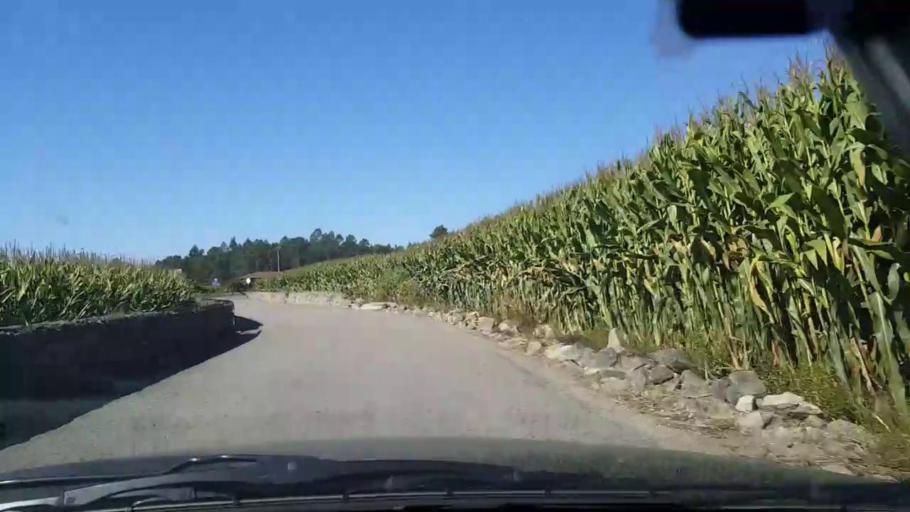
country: PT
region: Braga
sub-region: Vila Nova de Famalicao
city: Ribeirao
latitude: 41.3611
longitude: -8.6437
